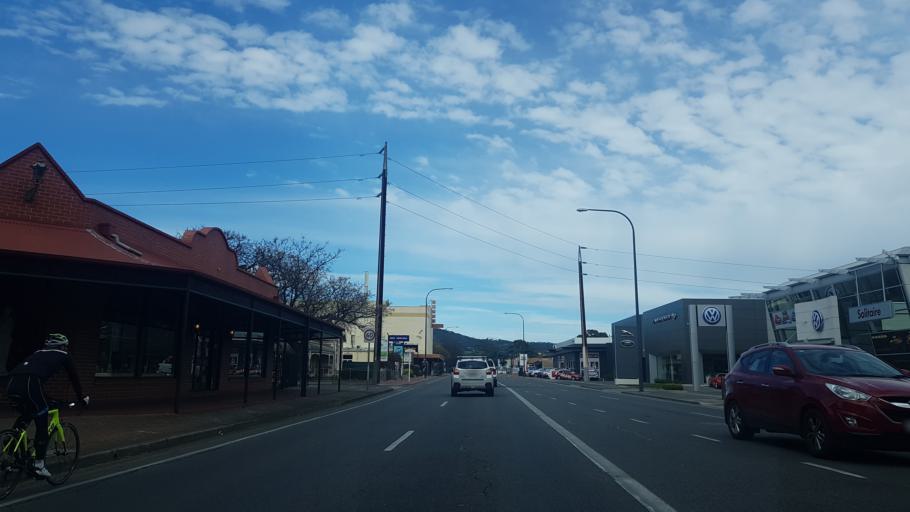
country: AU
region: South Australia
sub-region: Unley
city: Unley Park
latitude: -34.9663
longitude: 138.6087
